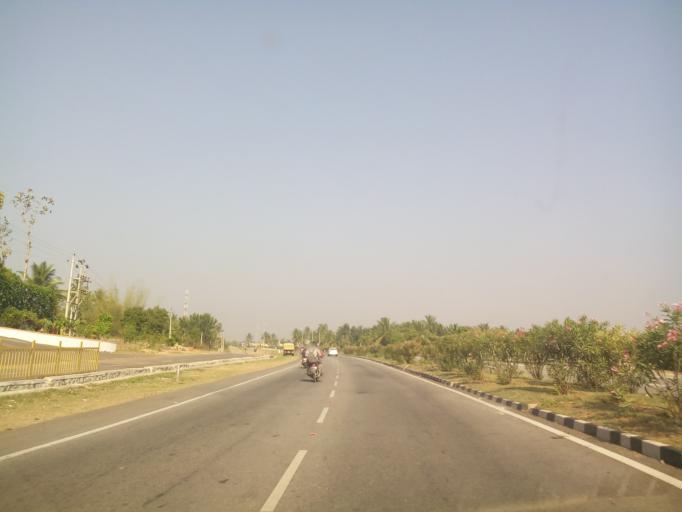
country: IN
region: Karnataka
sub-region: Bangalore Rural
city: Nelamangala
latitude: 13.0657
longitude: 77.3243
